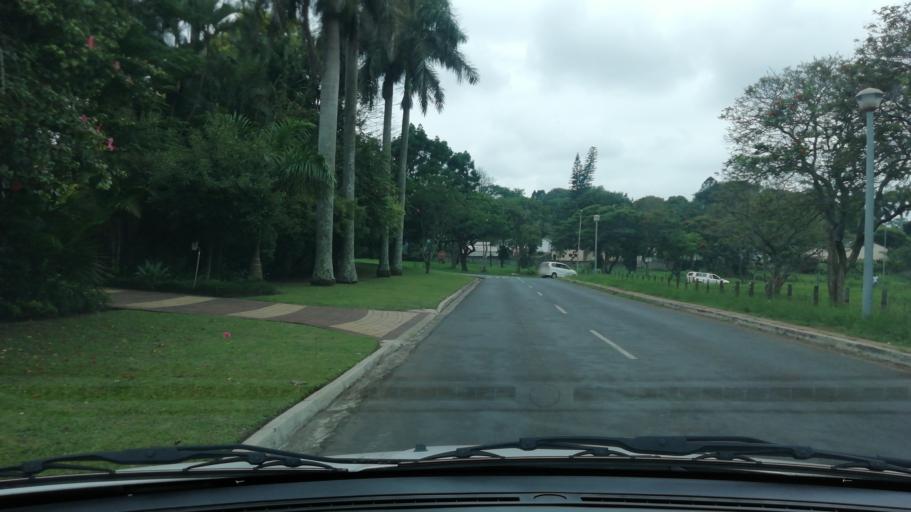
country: ZA
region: KwaZulu-Natal
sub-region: uThungulu District Municipality
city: Empangeni
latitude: -28.7577
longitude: 31.8908
